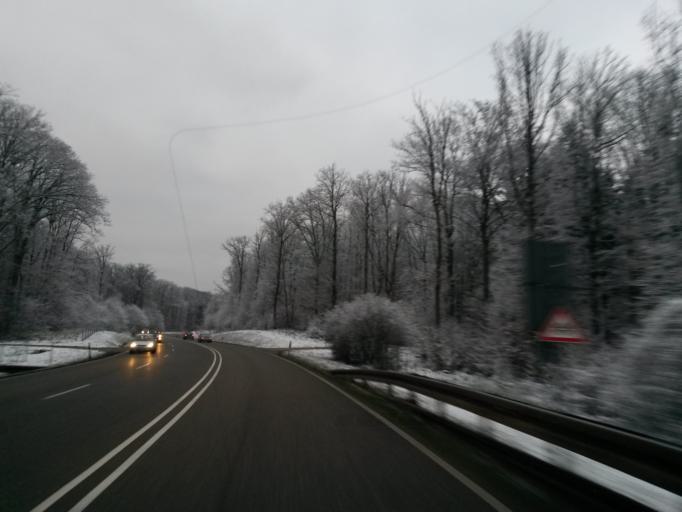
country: DE
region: Baden-Wuerttemberg
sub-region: Regierungsbezirk Stuttgart
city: Untergruppenbach
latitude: 49.1078
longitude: 9.2494
